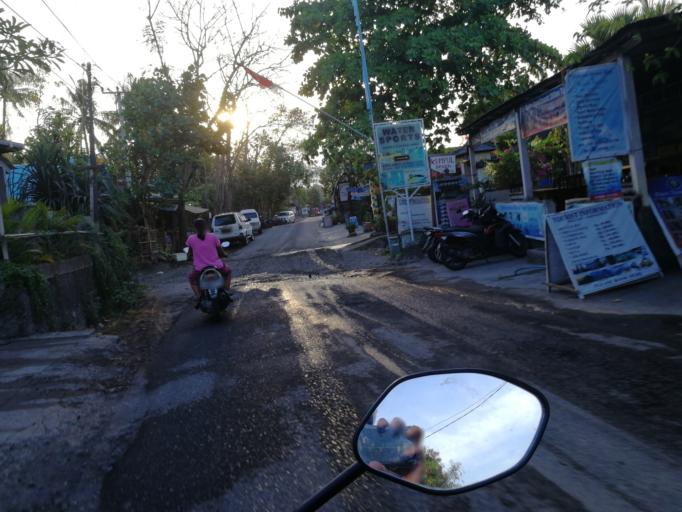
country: ID
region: Bali
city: Biaslantang Kaler
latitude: -8.3358
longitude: 115.6507
